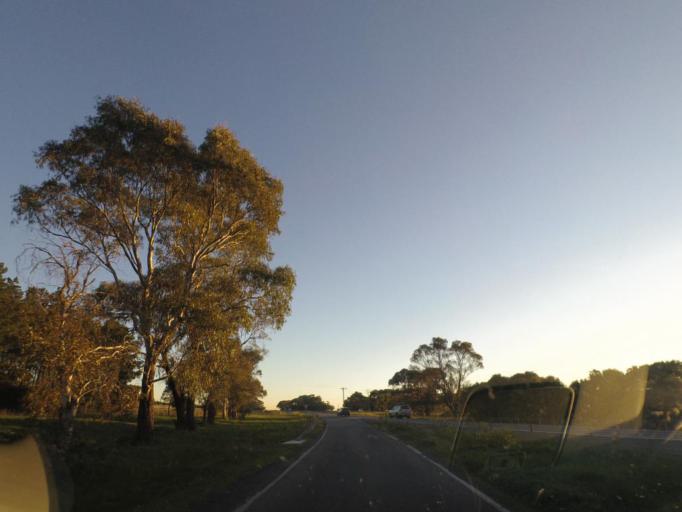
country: AU
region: Victoria
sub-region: Hume
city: Craigieburn
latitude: -37.4981
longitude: 144.9576
